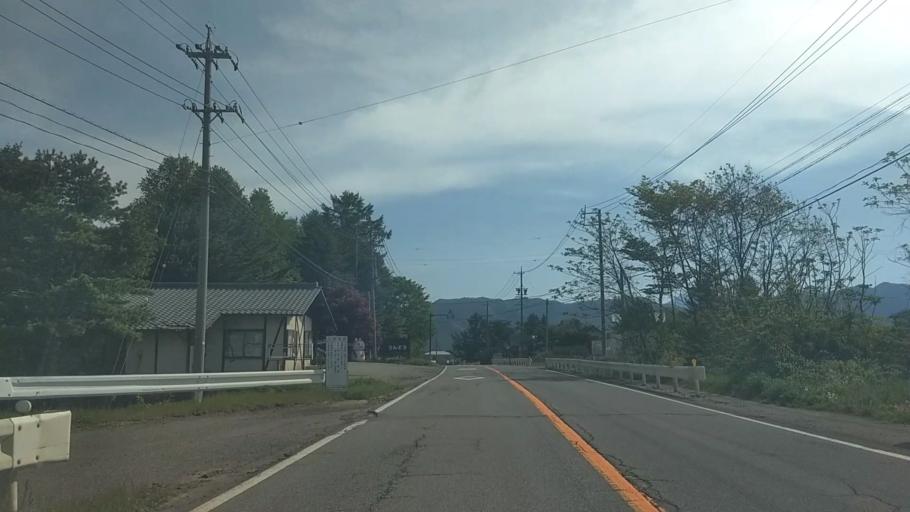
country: JP
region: Nagano
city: Saku
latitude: 35.9971
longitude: 138.4975
